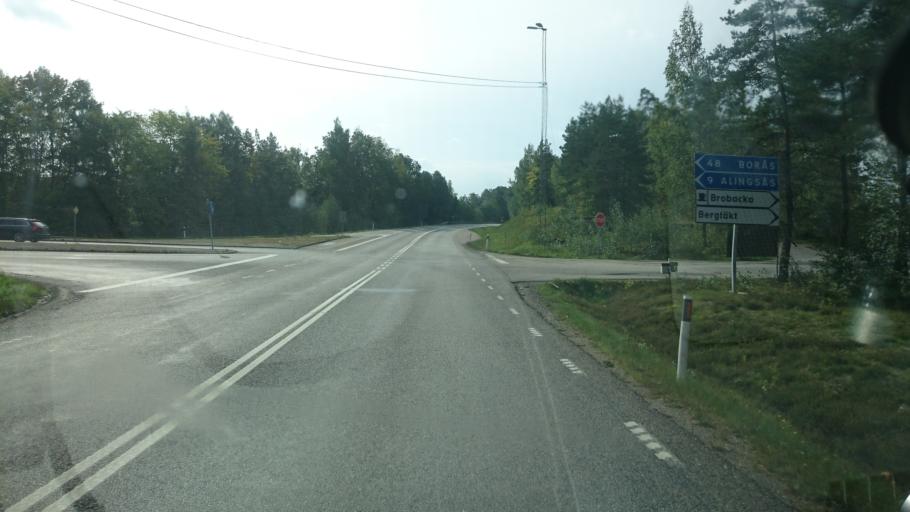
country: SE
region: Vaestra Goetaland
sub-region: Alingsas Kommun
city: Alingsas
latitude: 57.9760
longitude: 12.4332
